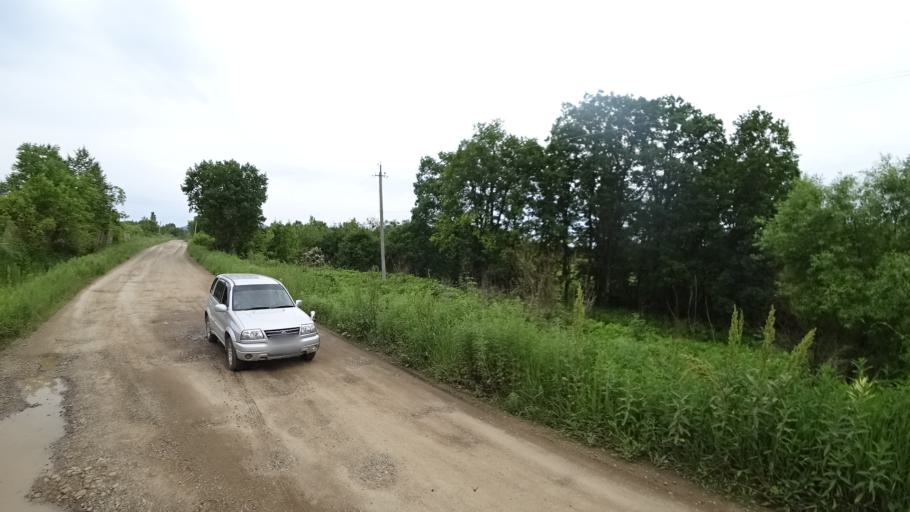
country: RU
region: Primorskiy
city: Arsen'yev
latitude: 44.1966
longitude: 133.3077
